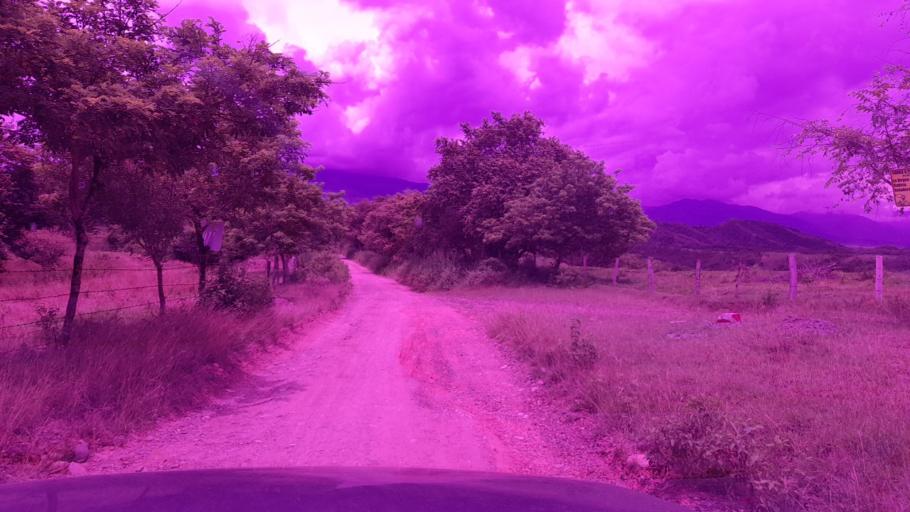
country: CO
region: Valle del Cauca
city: Andalucia
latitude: 4.1803
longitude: -76.1366
